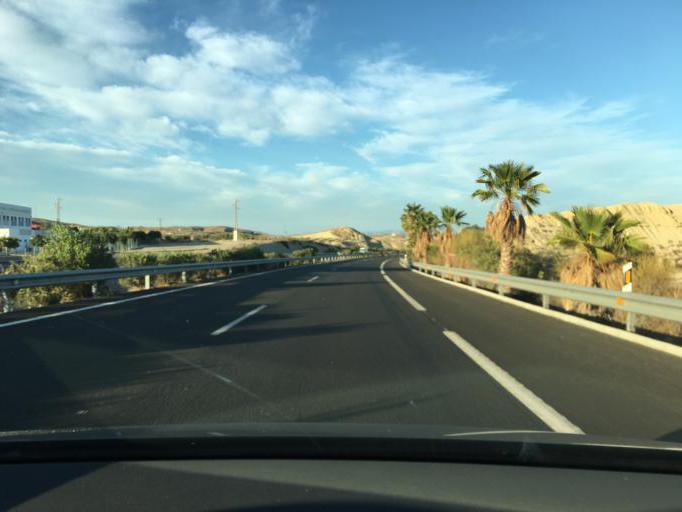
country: ES
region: Andalusia
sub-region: Provincia de Almeria
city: Bedar
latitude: 37.1725
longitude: -1.9436
